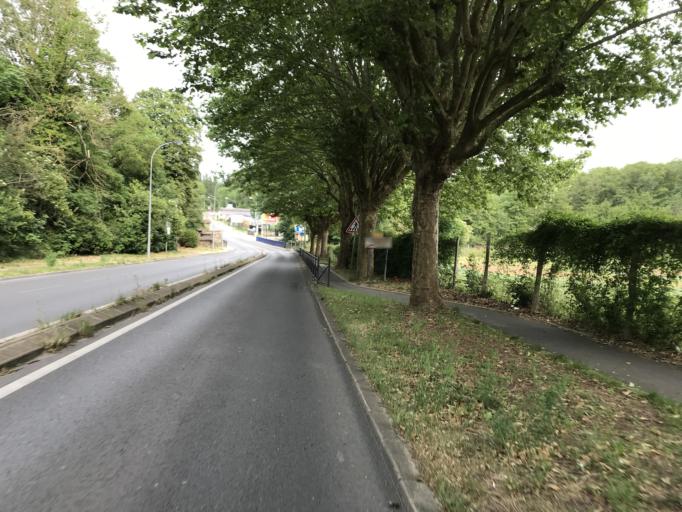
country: FR
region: Ile-de-France
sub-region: Departement de l'Essonne
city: Longpont-sur-Orge
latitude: 48.6342
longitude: 2.2923
